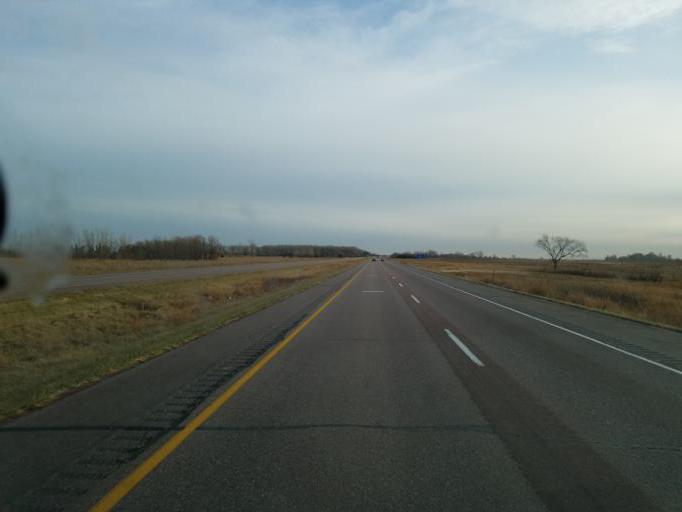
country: US
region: Nebraska
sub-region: Thurston County
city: Macy
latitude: 42.1445
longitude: -96.2151
